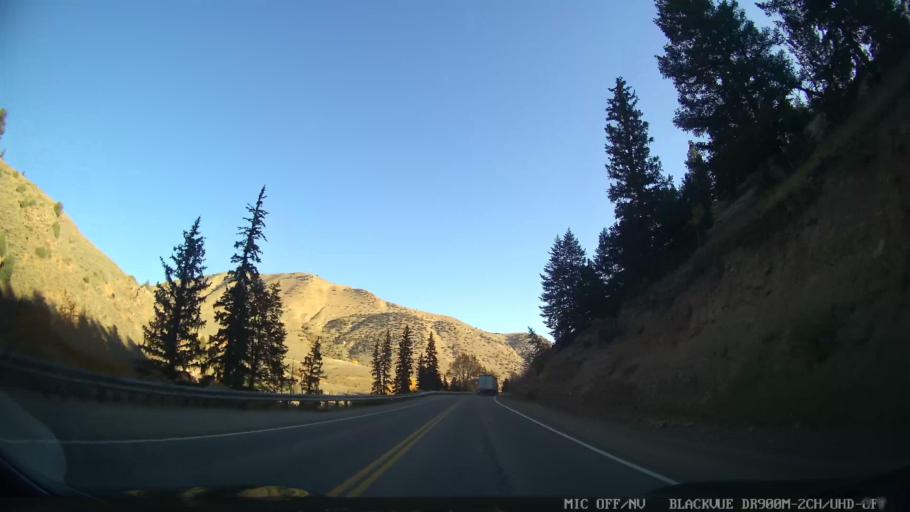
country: US
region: Colorado
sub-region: Grand County
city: Hot Sulphur Springs
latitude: 40.0687
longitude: -106.1130
